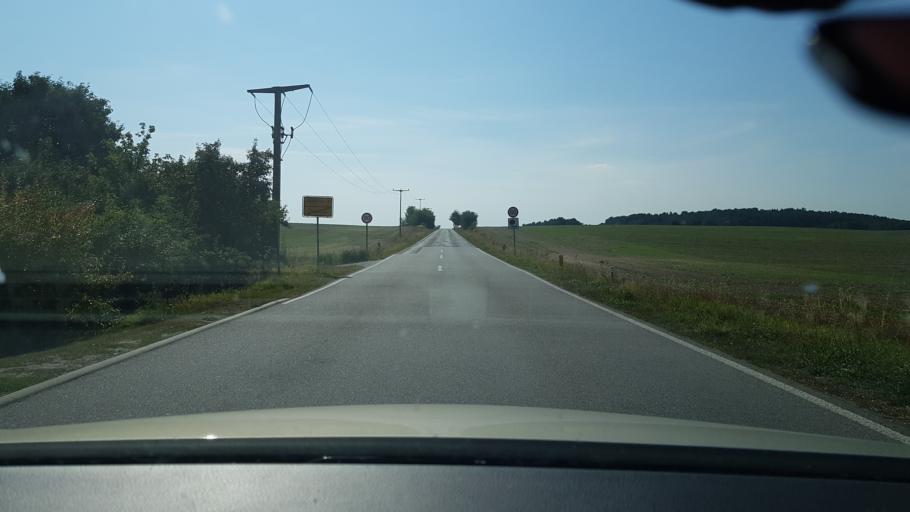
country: DE
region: Brandenburg
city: Lawitz
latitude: 52.1234
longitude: 14.5901
